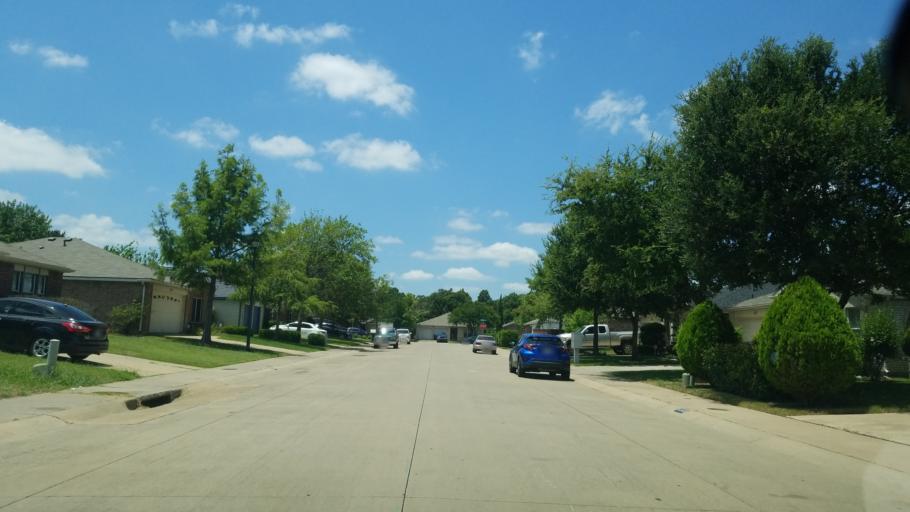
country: US
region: Texas
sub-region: Dallas County
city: Balch Springs
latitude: 32.7447
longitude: -96.7028
